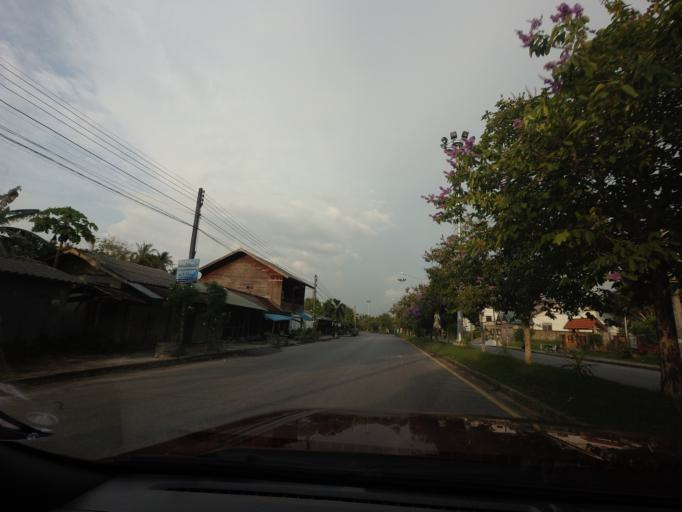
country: TH
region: Pattani
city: Khok Pho
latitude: 6.6770
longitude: 101.1427
